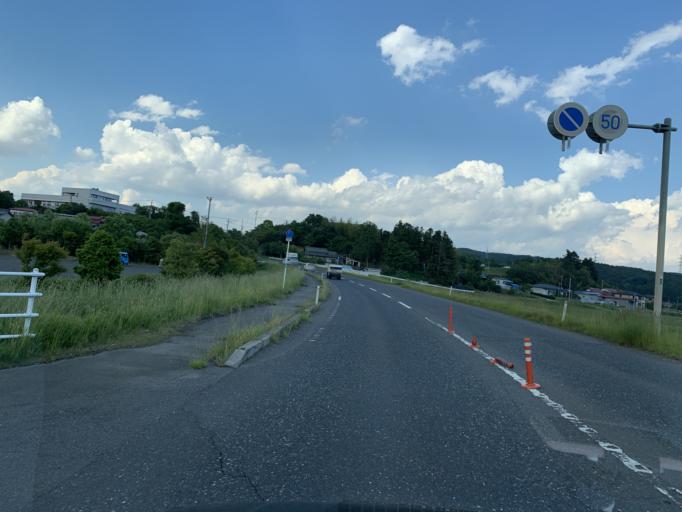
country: JP
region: Miyagi
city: Wakuya
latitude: 38.5369
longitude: 141.1496
